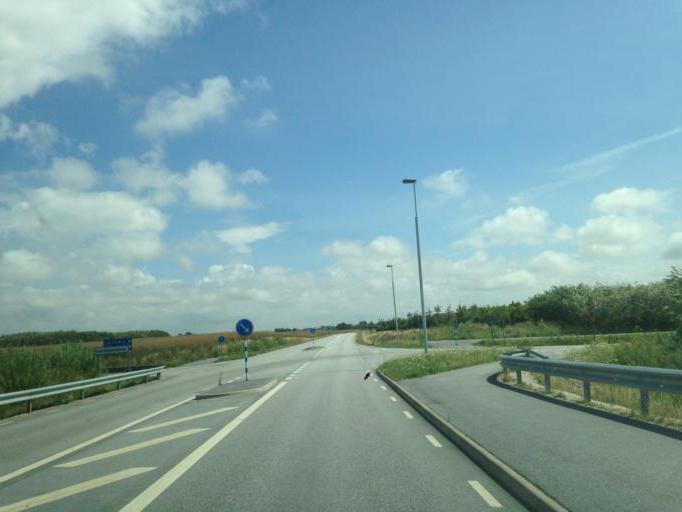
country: SE
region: Skane
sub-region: Trelleborgs Kommun
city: Skare
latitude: 55.4094
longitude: 13.0696
